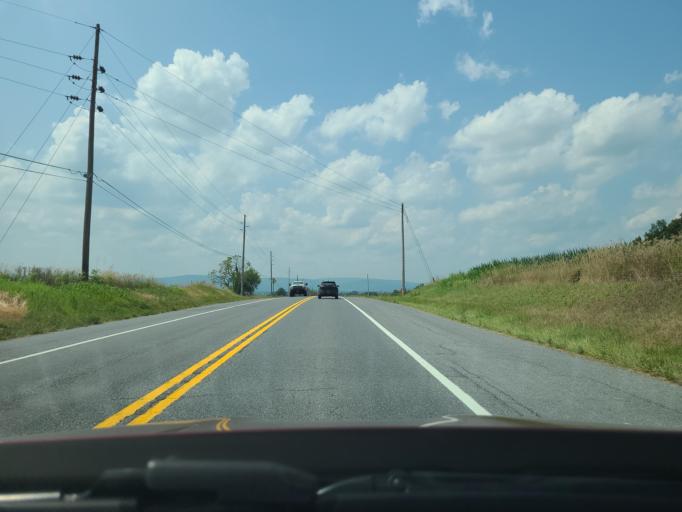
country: US
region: Maryland
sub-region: Frederick County
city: Woodsboro
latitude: 39.5474
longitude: -77.3288
